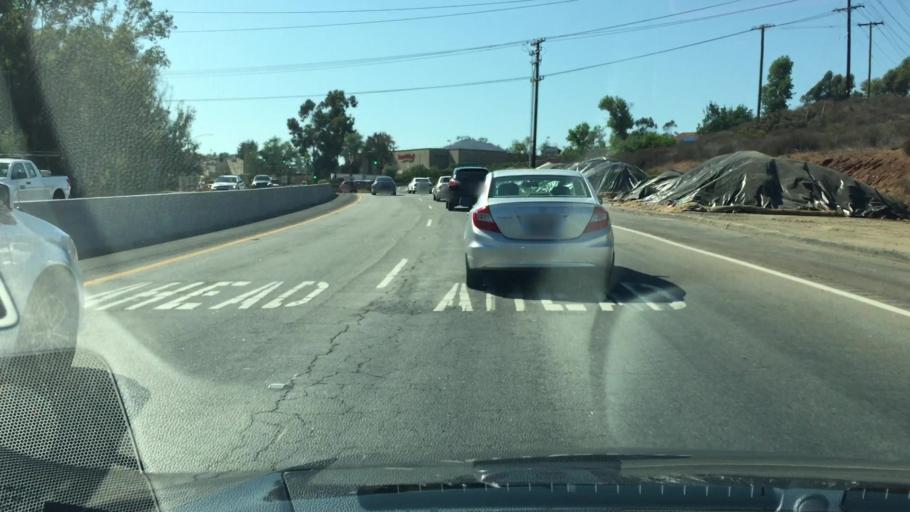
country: US
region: California
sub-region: San Diego County
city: Rancho San Diego
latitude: 32.7447
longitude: -116.9564
